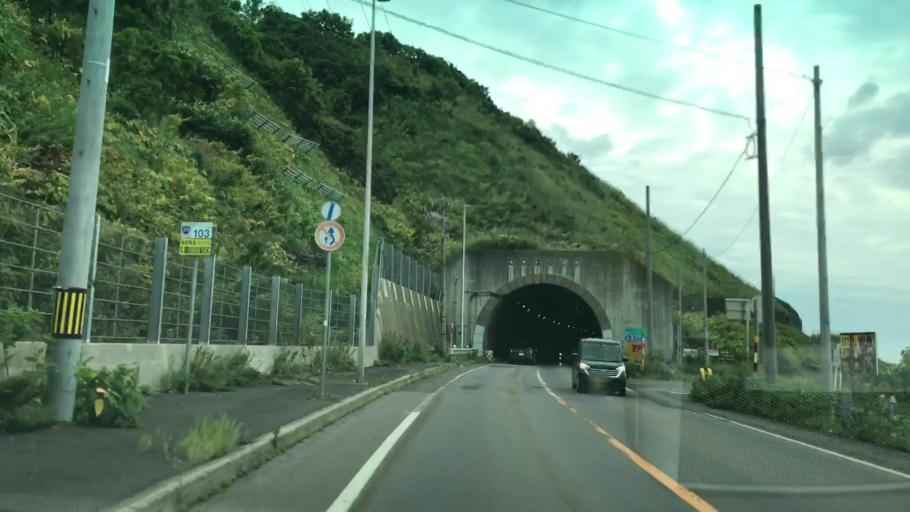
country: JP
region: Hokkaido
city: Iwanai
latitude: 42.9615
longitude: 140.4626
